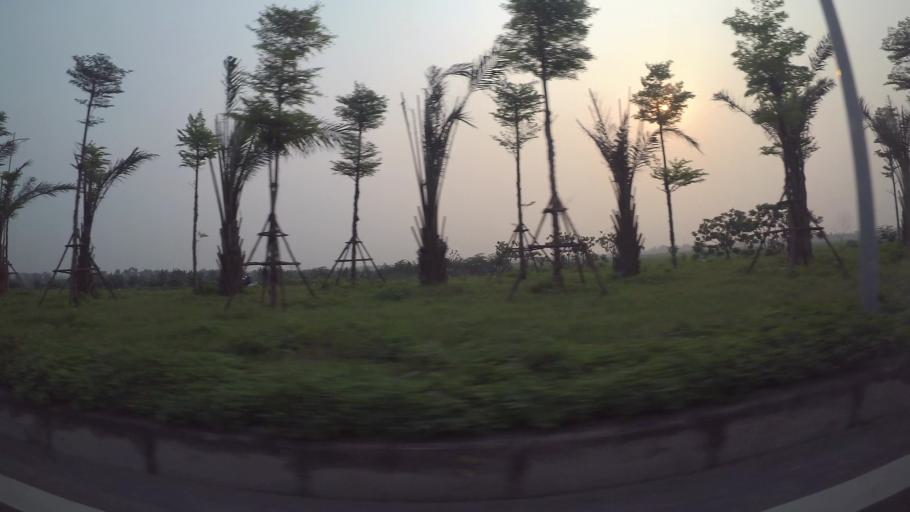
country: VN
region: Ha Noi
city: Kim Bai
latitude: 20.8776
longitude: 105.8010
